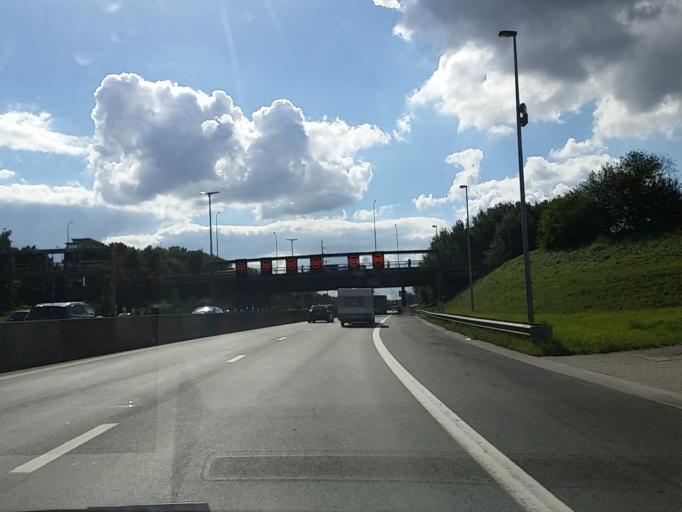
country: BE
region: Flanders
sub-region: Provincie Antwerpen
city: Borsbeek
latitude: 51.2142
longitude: 4.4480
